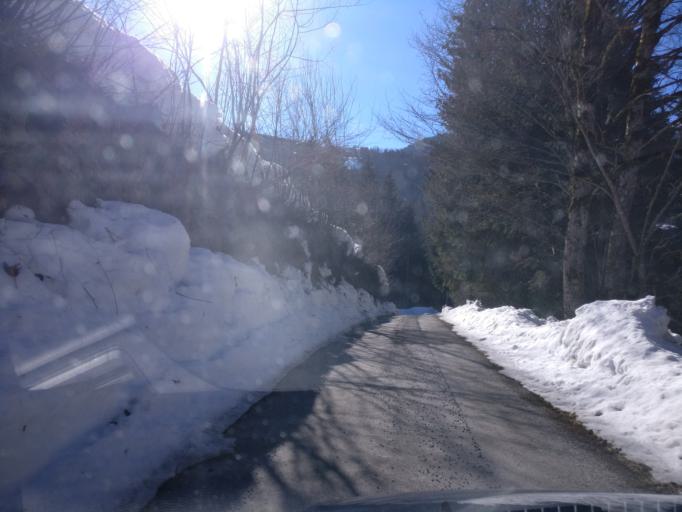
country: AT
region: Salzburg
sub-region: Politischer Bezirk Sankt Johann im Pongau
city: Wagrain
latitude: 47.3364
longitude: 13.2528
